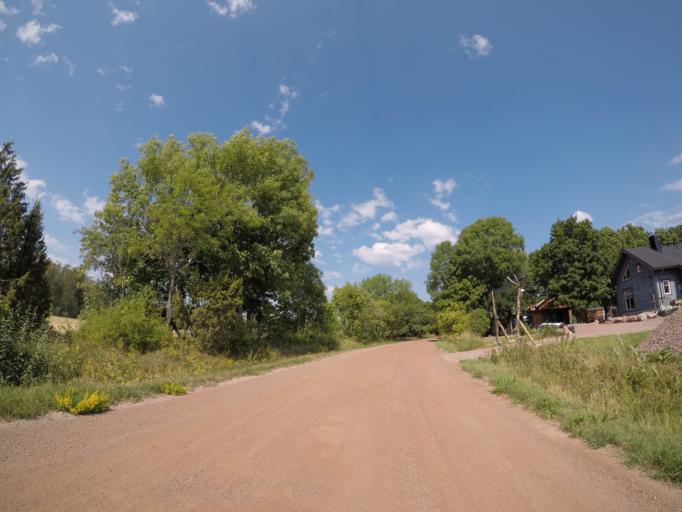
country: AX
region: Alands landsbygd
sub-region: Finstroem
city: Finstroem
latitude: 60.2142
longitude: 19.8560
